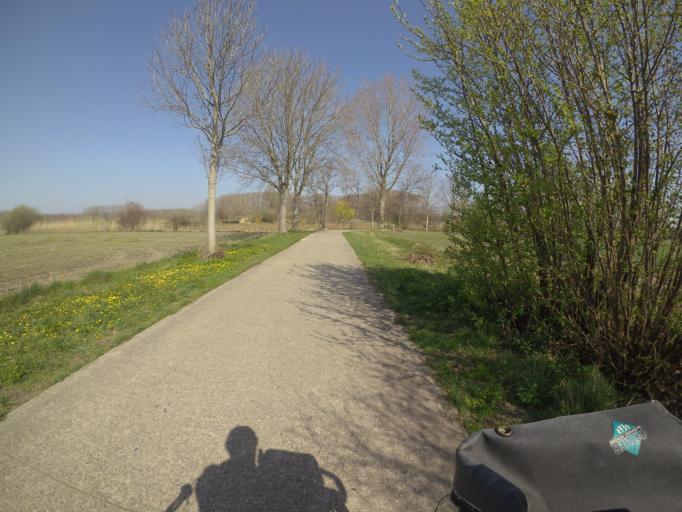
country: NL
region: North Brabant
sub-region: Gemeente Boxtel
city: Boxtel
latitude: 51.5762
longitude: 5.3859
